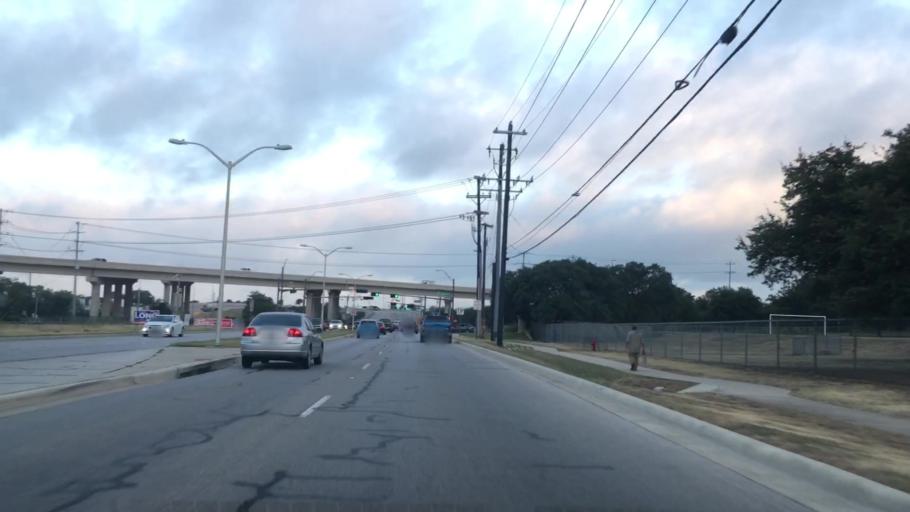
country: US
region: Texas
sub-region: Williamson County
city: Cedar Park
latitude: 30.5031
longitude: -97.8066
